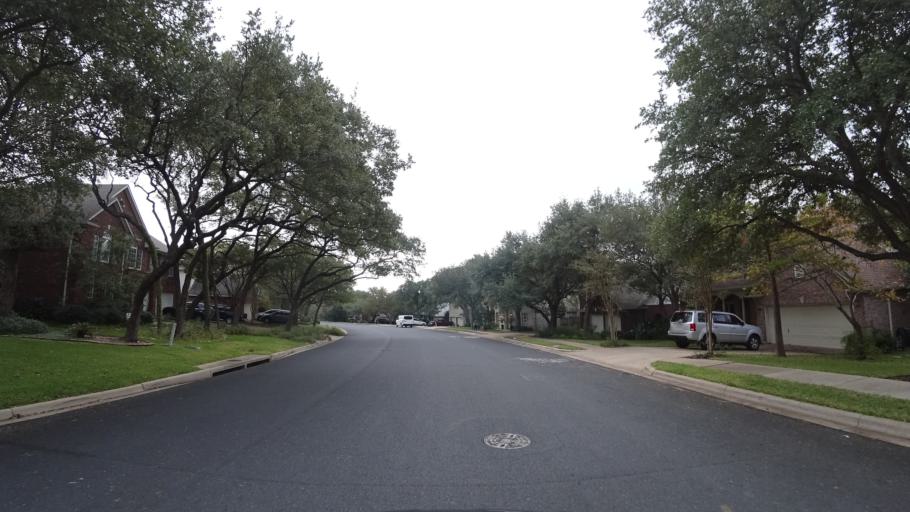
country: US
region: Texas
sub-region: Travis County
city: Shady Hollow
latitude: 30.1871
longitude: -97.8963
